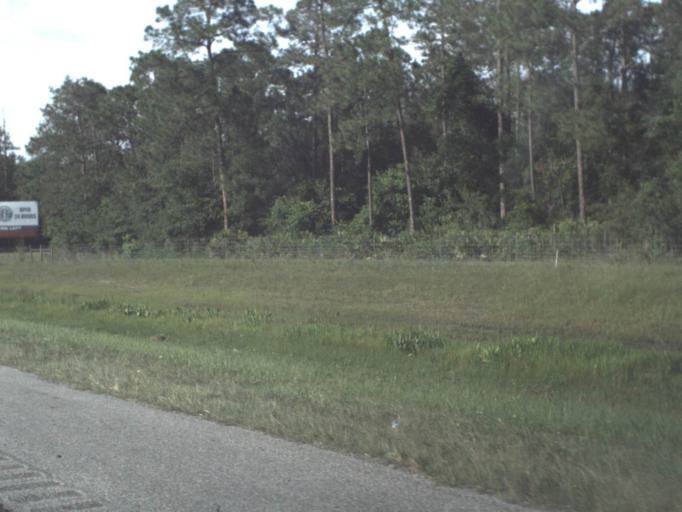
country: US
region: Florida
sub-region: Saint Johns County
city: Fruit Cove
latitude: 30.0575
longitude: -81.4975
